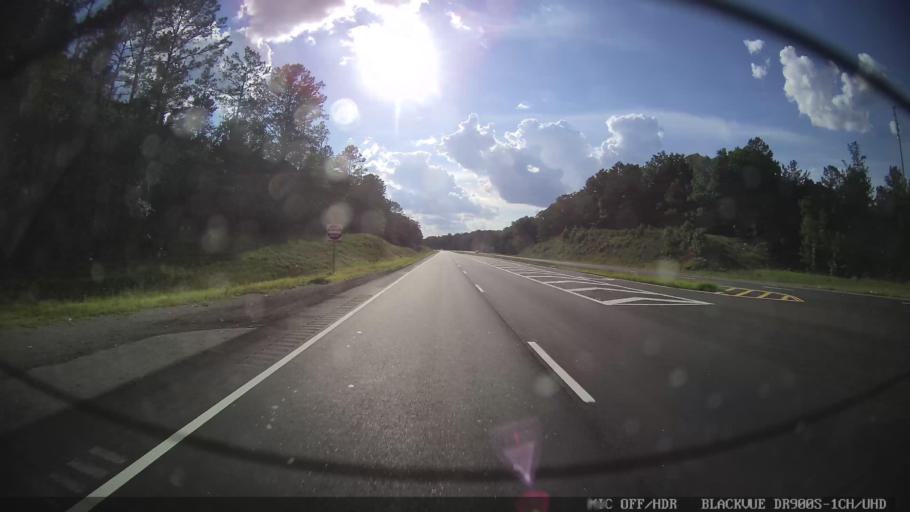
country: US
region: Georgia
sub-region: Floyd County
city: Rome
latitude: 34.2073
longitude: -85.0459
